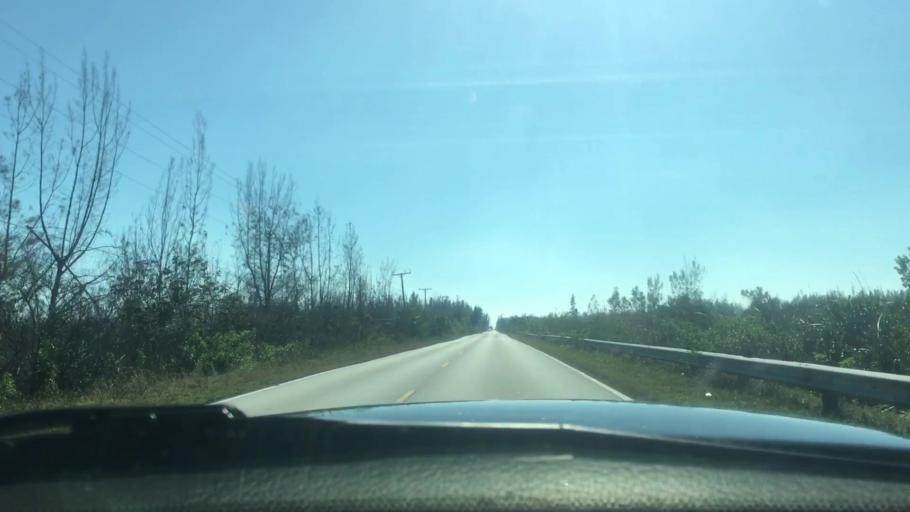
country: US
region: Florida
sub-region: Miami-Dade County
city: Florida City
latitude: 25.4256
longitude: -80.4681
